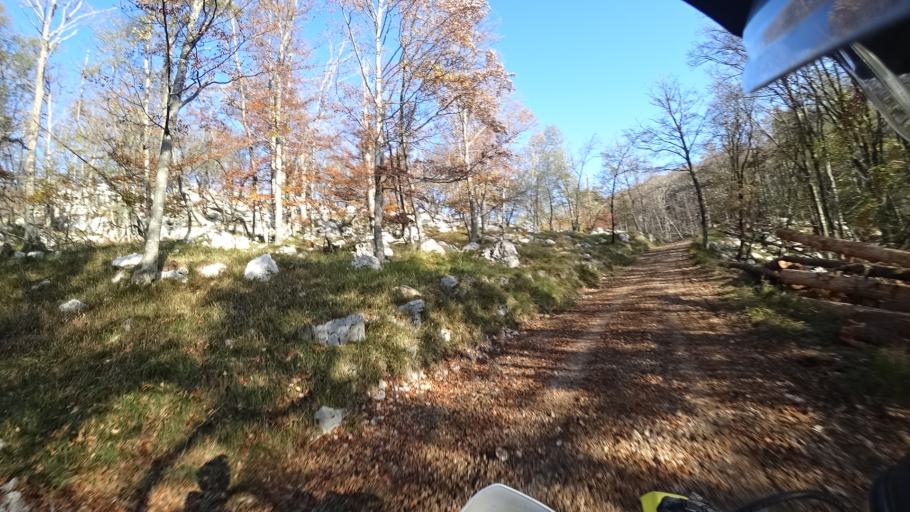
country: HR
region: Primorsko-Goranska
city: Klana
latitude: 45.4811
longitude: 14.4299
